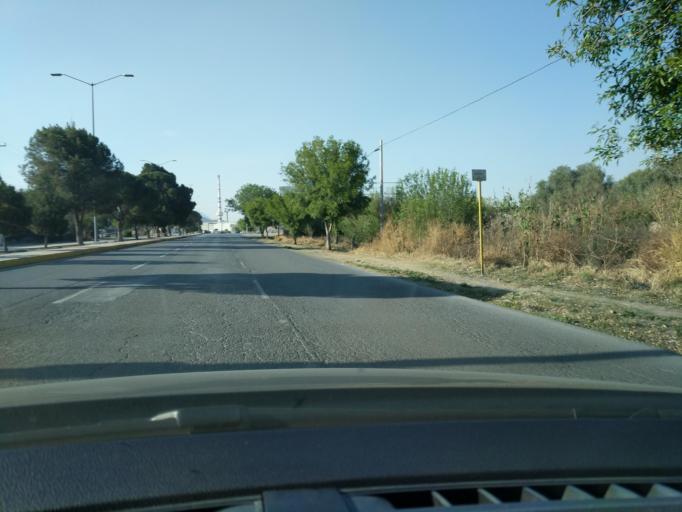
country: MX
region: Coahuila
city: Saltillo
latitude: 25.4756
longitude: -100.9831
